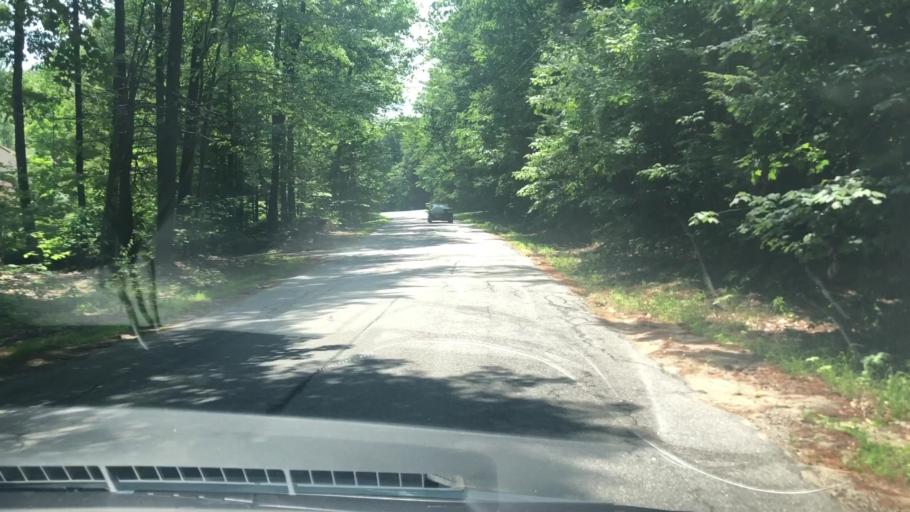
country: US
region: New Hampshire
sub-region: Hillsborough County
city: Milford
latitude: 42.8758
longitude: -71.6145
